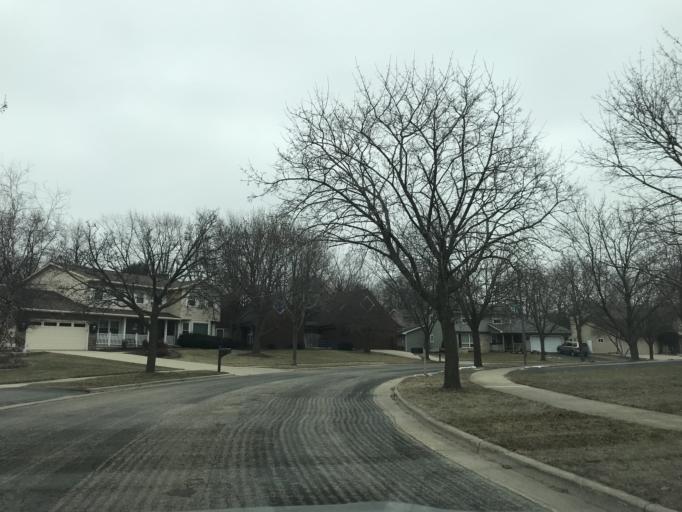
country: US
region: Wisconsin
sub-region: Dane County
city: Monona
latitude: 43.0981
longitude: -89.2928
